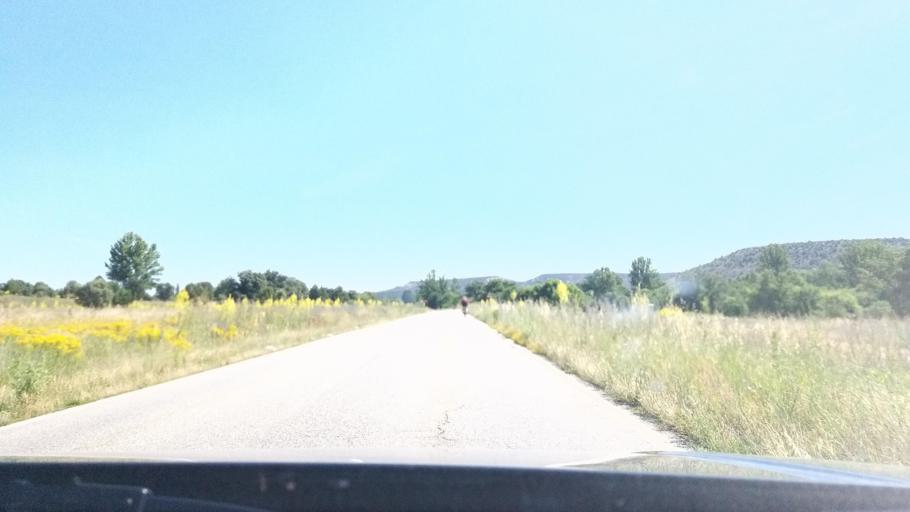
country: ES
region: Castille and Leon
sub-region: Provincia de Segovia
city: Arahuetes
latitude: 41.1360
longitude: -3.8342
